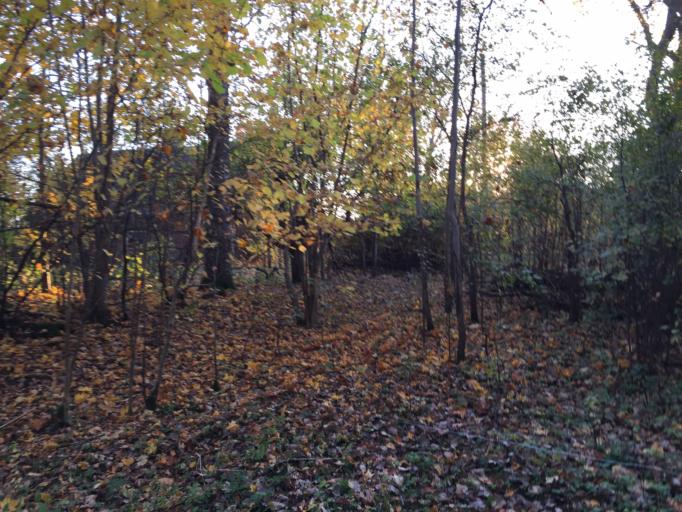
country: LV
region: Vainode
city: Vainode
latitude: 56.5114
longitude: 21.8258
